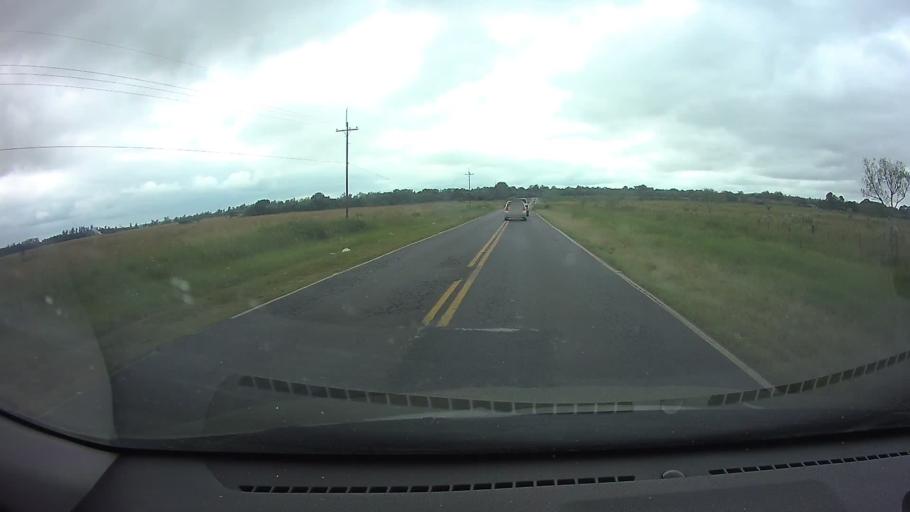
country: PY
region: Central
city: Nueva Italia
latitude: -25.5615
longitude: -57.5013
